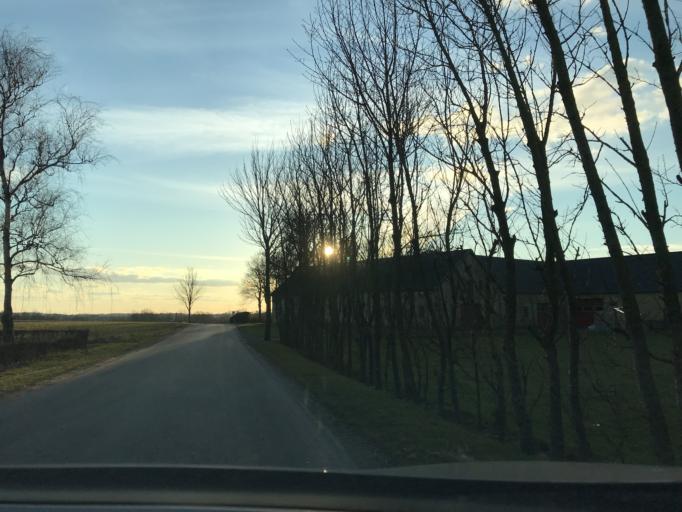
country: DK
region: South Denmark
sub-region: Middelfart Kommune
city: Ejby
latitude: 55.4629
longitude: 9.9298
